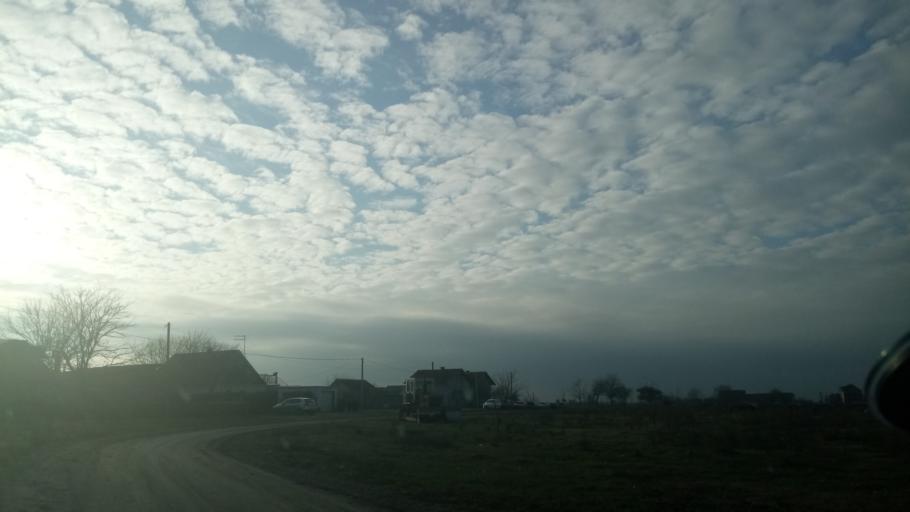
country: RS
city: Vojka
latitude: 44.9324
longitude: 20.1394
